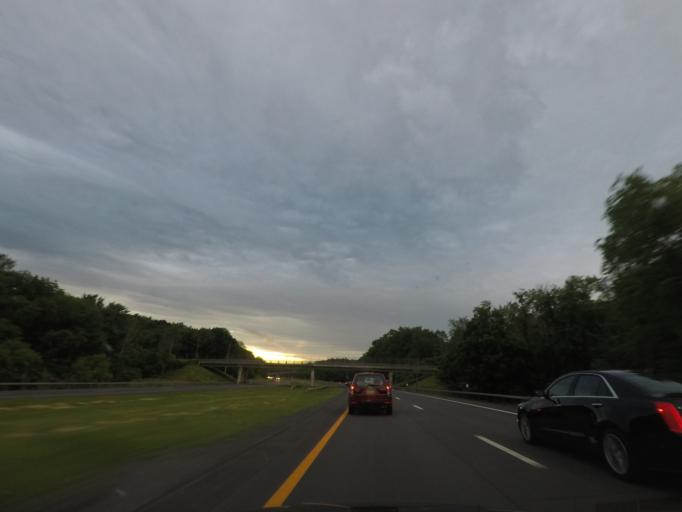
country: US
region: New York
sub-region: Columbia County
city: Chatham
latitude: 42.4440
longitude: -73.5588
